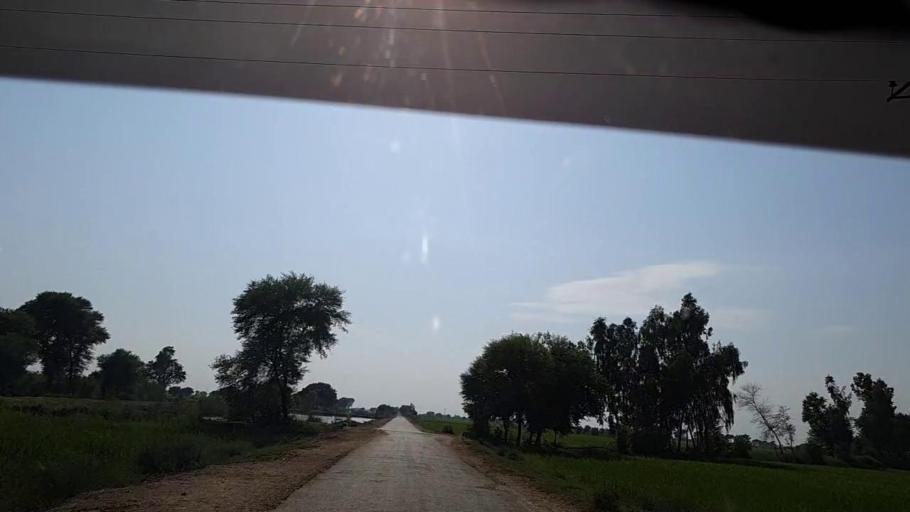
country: PK
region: Sindh
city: Shikarpur
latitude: 28.0839
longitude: 68.6575
